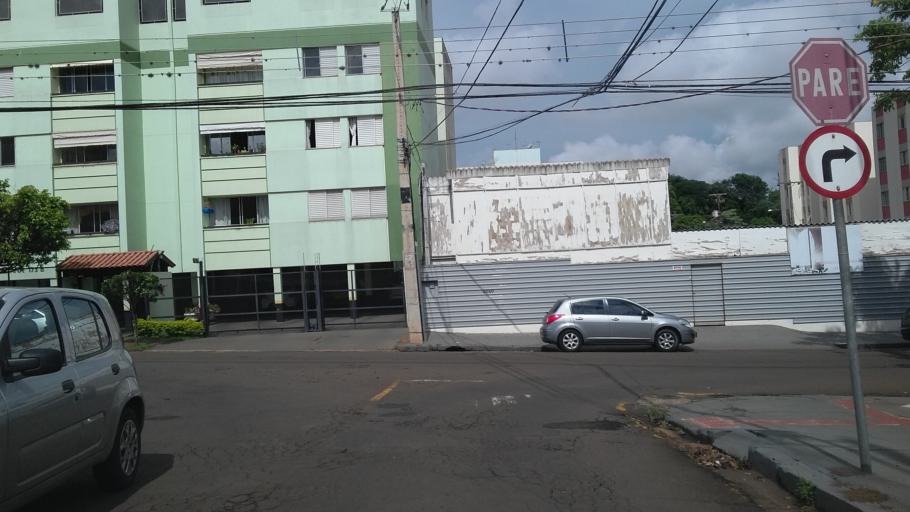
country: BR
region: Parana
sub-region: Londrina
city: Londrina
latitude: -23.3035
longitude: -51.1763
